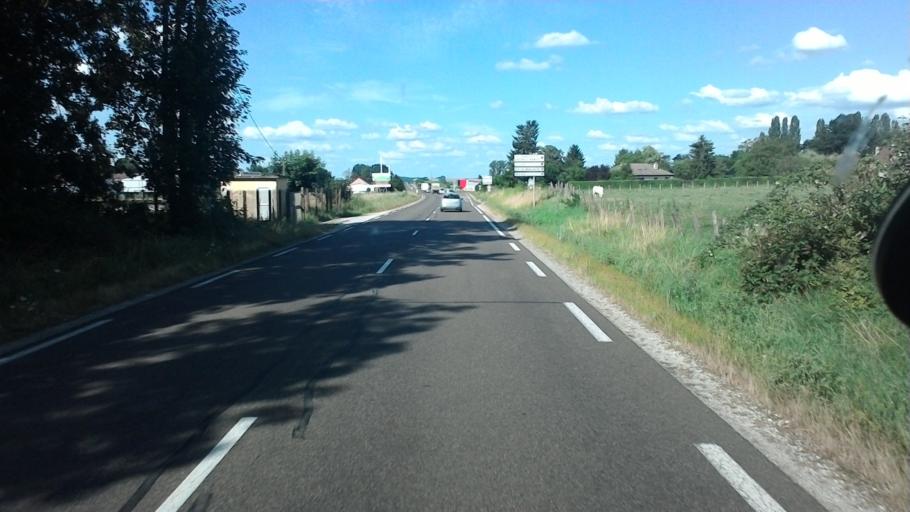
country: FR
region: Franche-Comte
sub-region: Departement de la Haute-Saone
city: Gy
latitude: 47.4102
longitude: 5.8085
